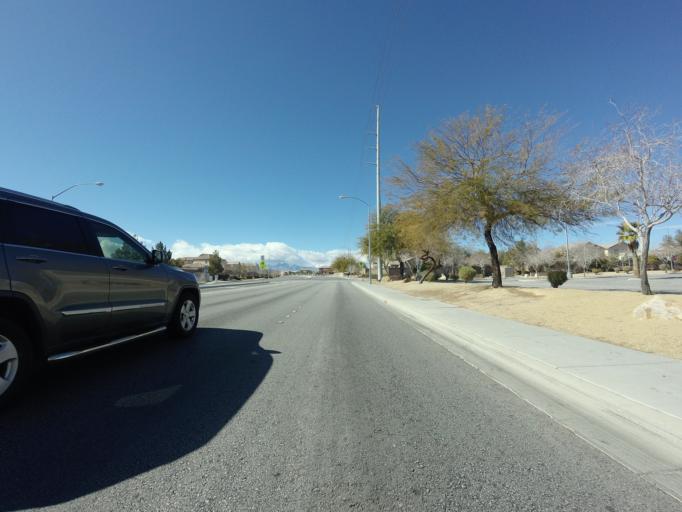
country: US
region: Nevada
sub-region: Clark County
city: Nellis Air Force Base
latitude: 36.2691
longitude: -115.1071
